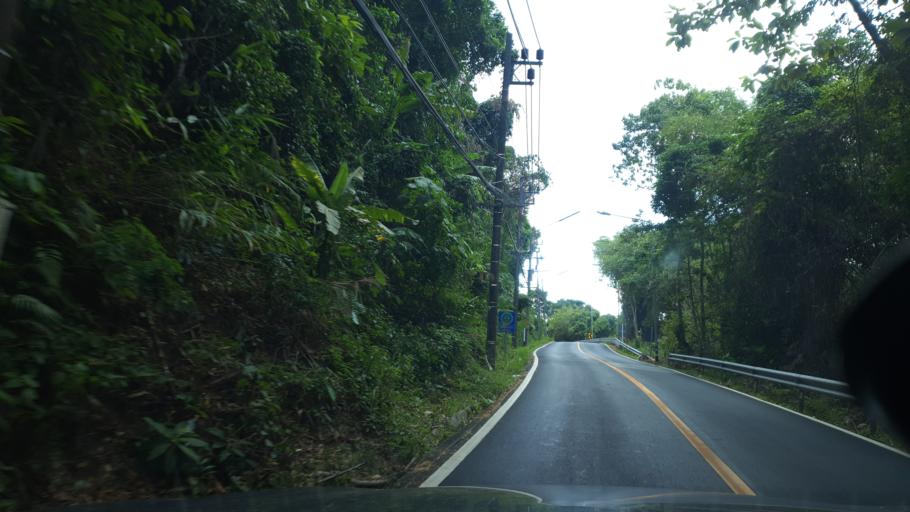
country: TH
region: Phuket
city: Thalang
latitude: 8.0454
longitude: 98.2777
